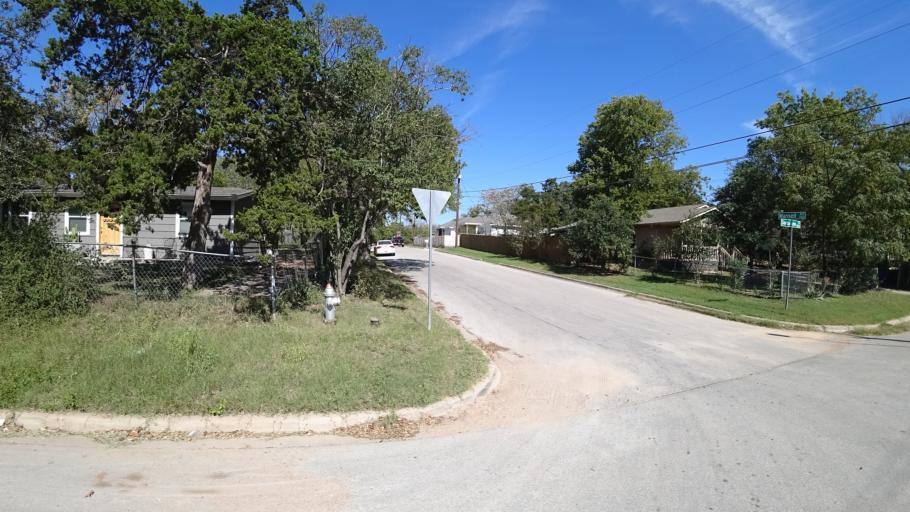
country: US
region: Texas
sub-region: Travis County
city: Austin
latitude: 30.2749
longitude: -97.6871
